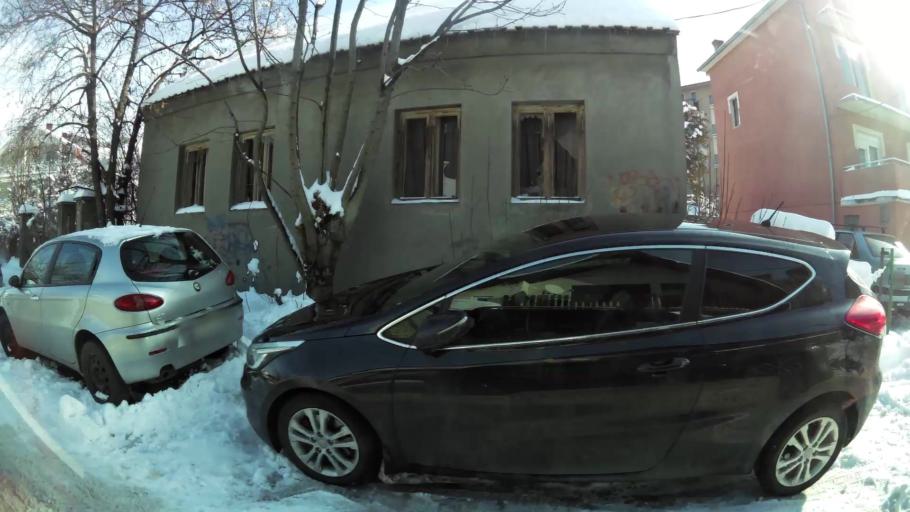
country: RS
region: Central Serbia
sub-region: Belgrade
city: Palilula
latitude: 44.7959
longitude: 20.5289
